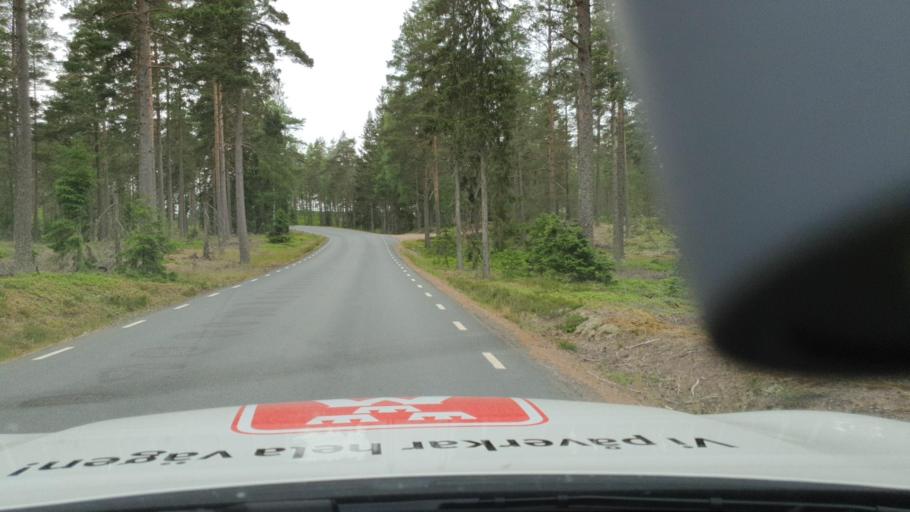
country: SE
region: Vaestra Goetaland
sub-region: Tidaholms Kommun
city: Tidaholm
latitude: 58.0987
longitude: 14.1298
